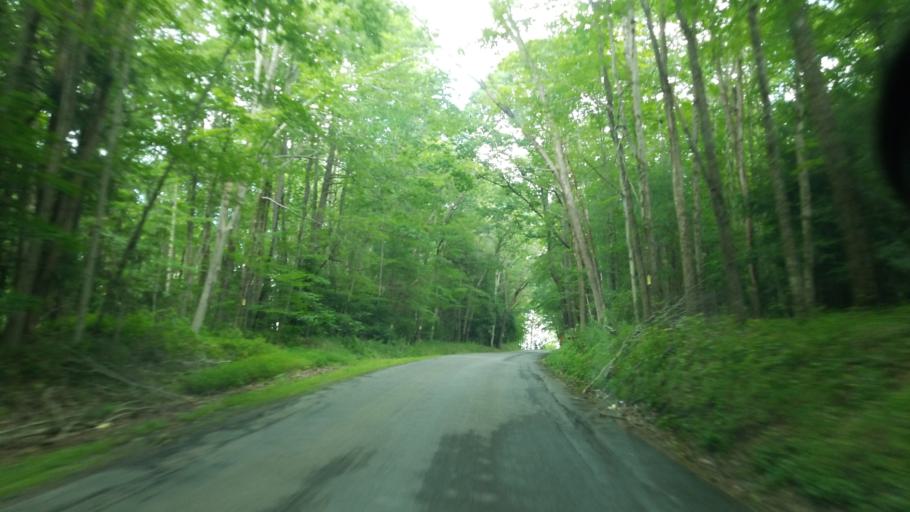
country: US
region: Pennsylvania
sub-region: Jefferson County
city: Brookville
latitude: 41.2269
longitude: -79.1087
